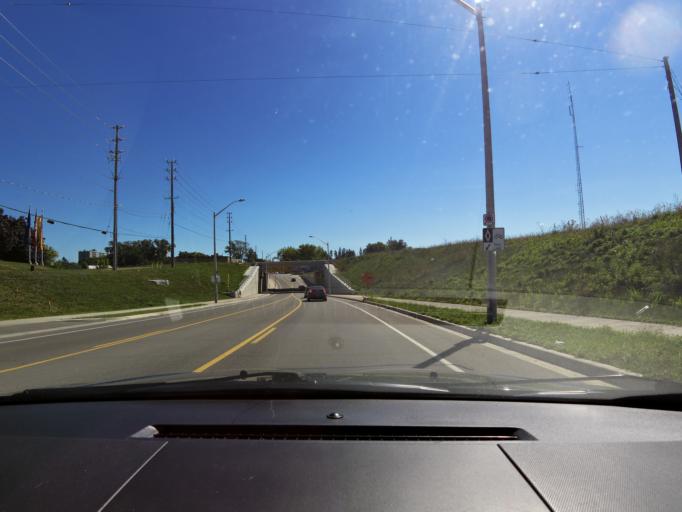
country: CA
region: Ontario
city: Burlington
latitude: 43.3251
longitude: -79.8374
